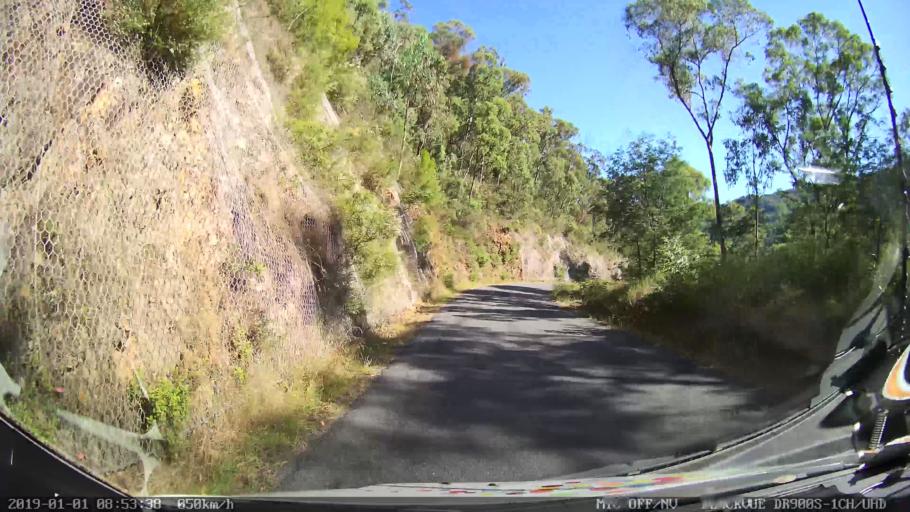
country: AU
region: New South Wales
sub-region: Snowy River
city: Jindabyne
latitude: -36.2645
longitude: 148.1898
